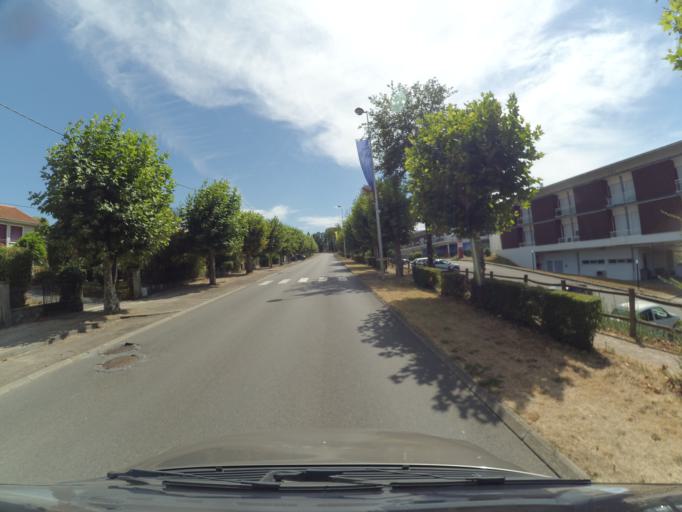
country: FR
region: Poitou-Charentes
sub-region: Departement de la Charente
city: Confolens
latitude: 46.0076
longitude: 0.6723
